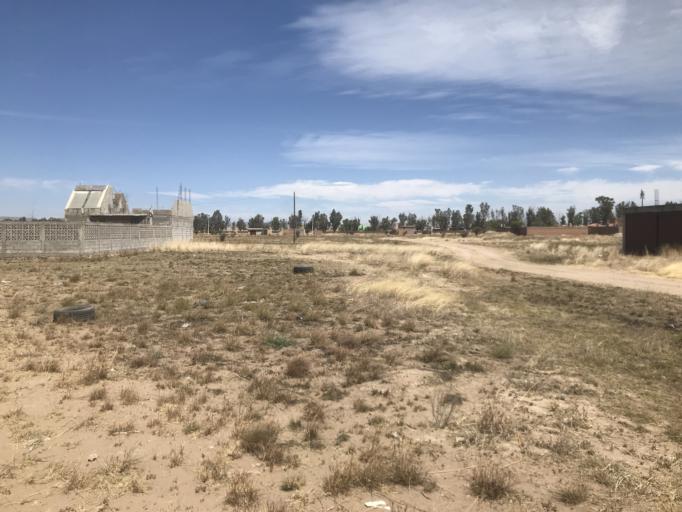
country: MX
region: Durango
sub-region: Durango
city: Sebastian Lerdo de Tejada
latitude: 23.9791
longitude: -104.6543
